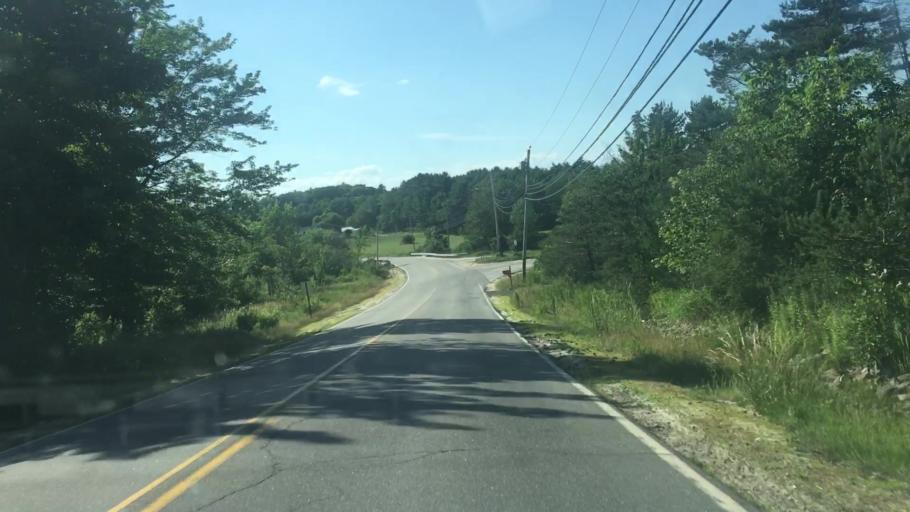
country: US
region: Maine
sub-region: York County
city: Buxton
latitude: 43.6287
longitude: -70.5537
